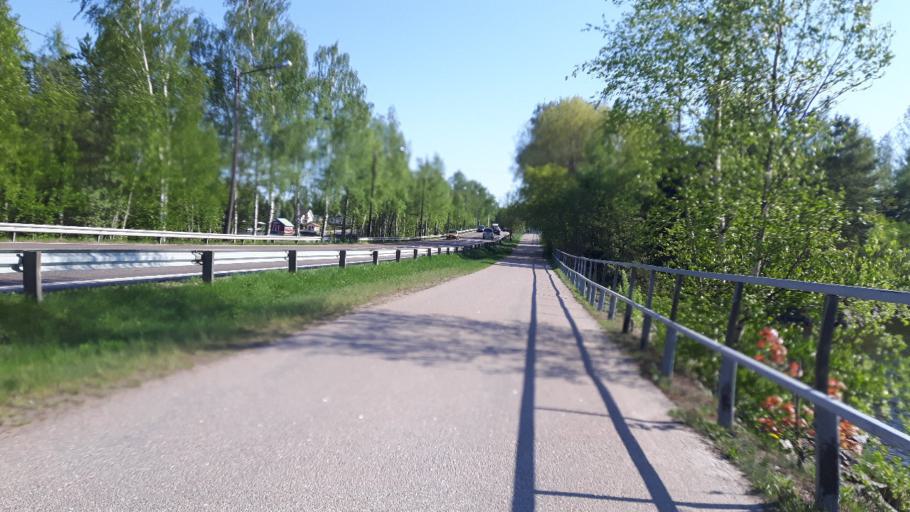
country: FI
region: Kymenlaakso
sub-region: Kotka-Hamina
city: Kotka
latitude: 60.4710
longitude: 26.8776
